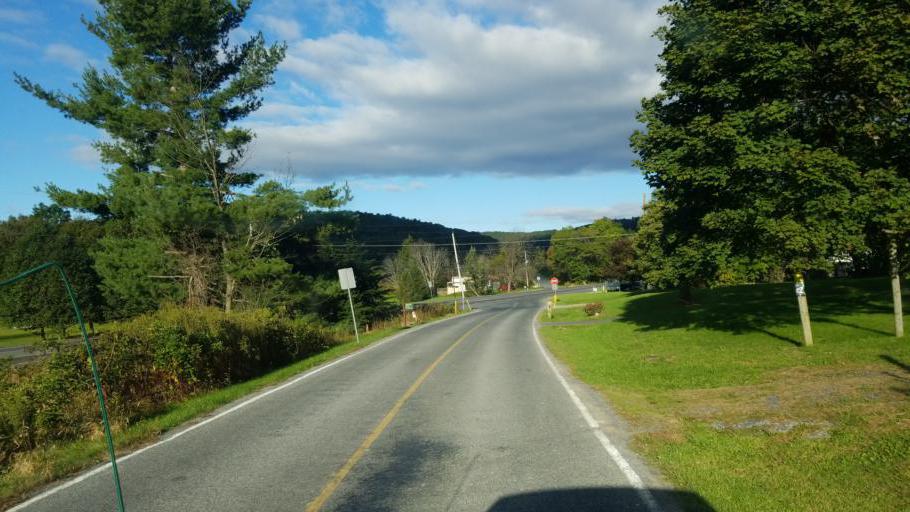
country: US
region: Pennsylvania
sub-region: Adams County
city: Biglerville
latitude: 39.8893
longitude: -77.3471
